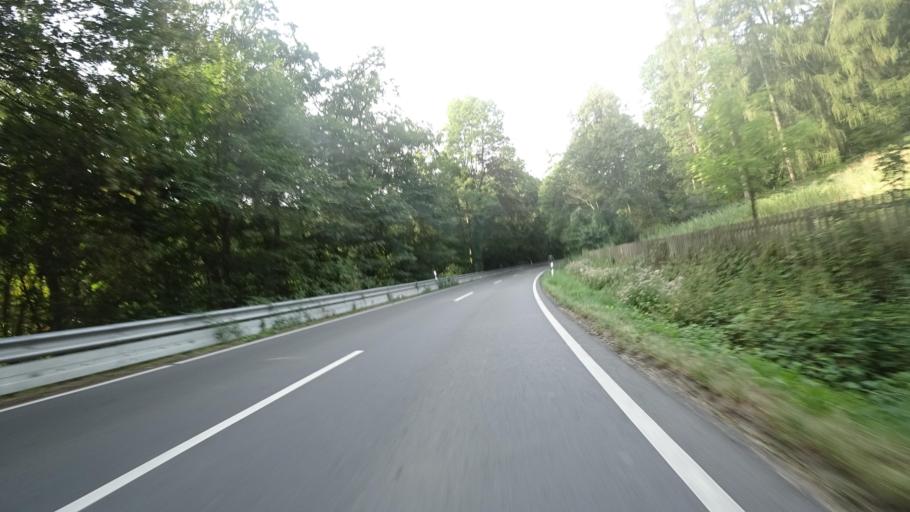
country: DE
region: North Rhine-Westphalia
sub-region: Regierungsbezirk Detmold
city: Steinhagen
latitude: 52.0189
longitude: 8.4519
